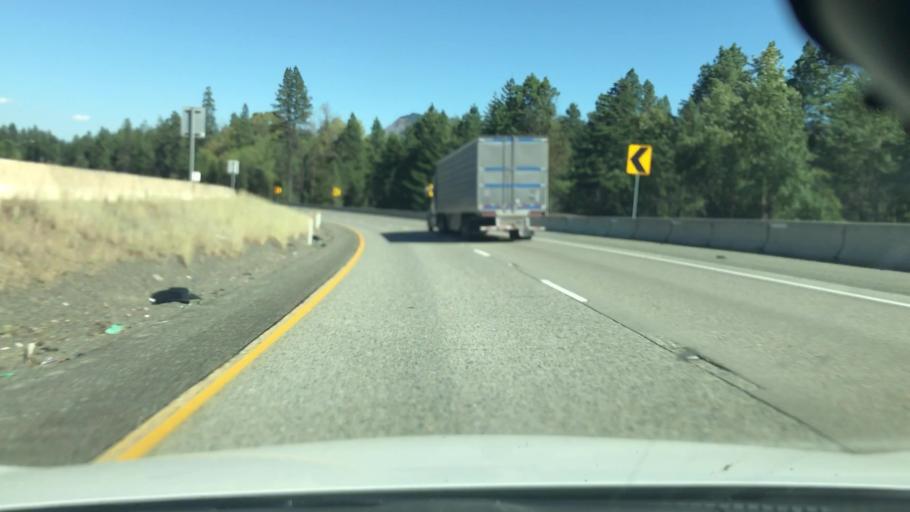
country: US
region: Washington
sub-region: Kittitas County
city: Cle Elum
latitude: 47.1825
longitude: -121.0396
